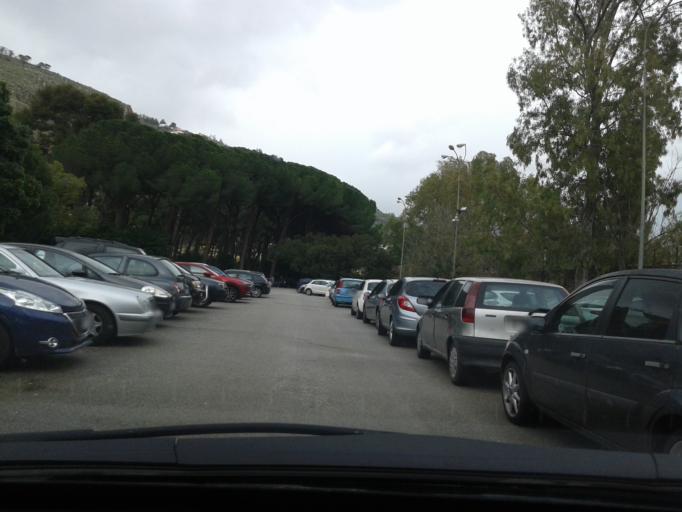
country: IT
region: Sicily
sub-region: Palermo
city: Monreale
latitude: 38.0924
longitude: 13.3123
